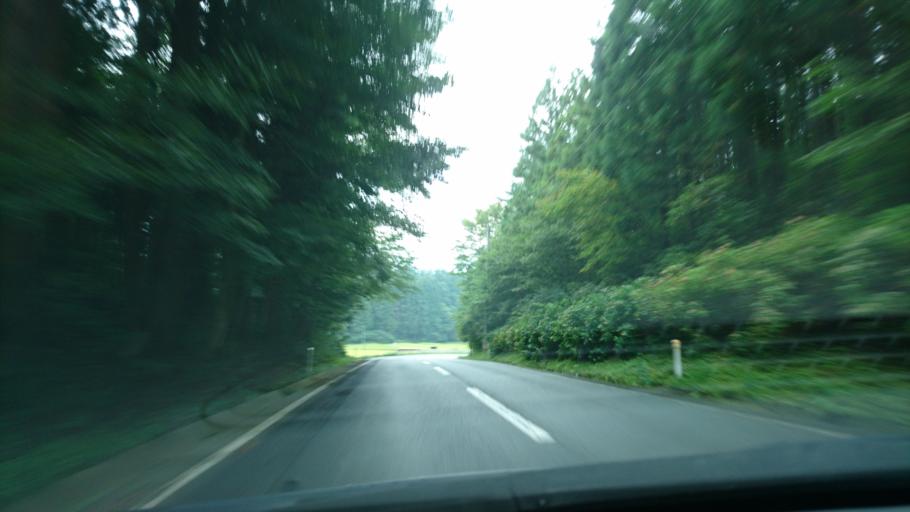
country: JP
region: Iwate
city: Ichinoseki
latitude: 39.0233
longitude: 141.2030
